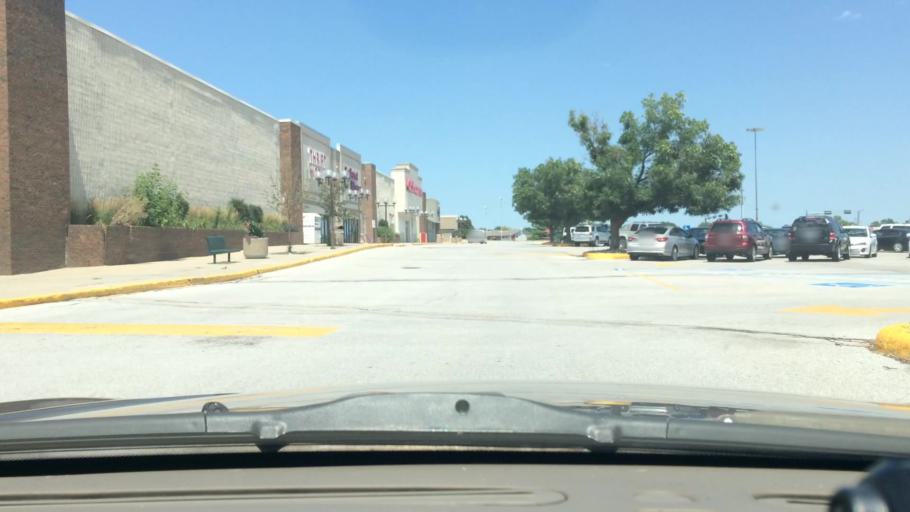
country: US
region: Nebraska
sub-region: Sarpy County
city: La Vista
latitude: 41.1782
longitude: -96.0452
